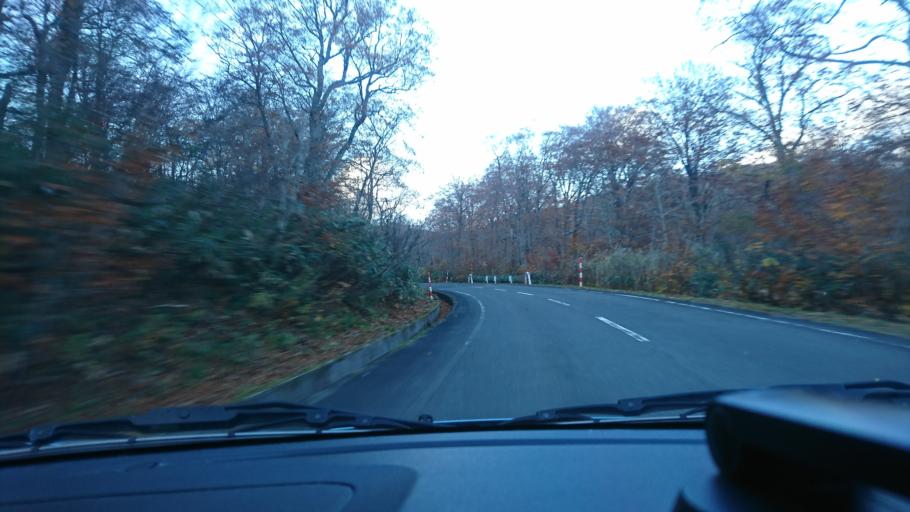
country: JP
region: Akita
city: Yuzawa
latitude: 38.9277
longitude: 140.7289
